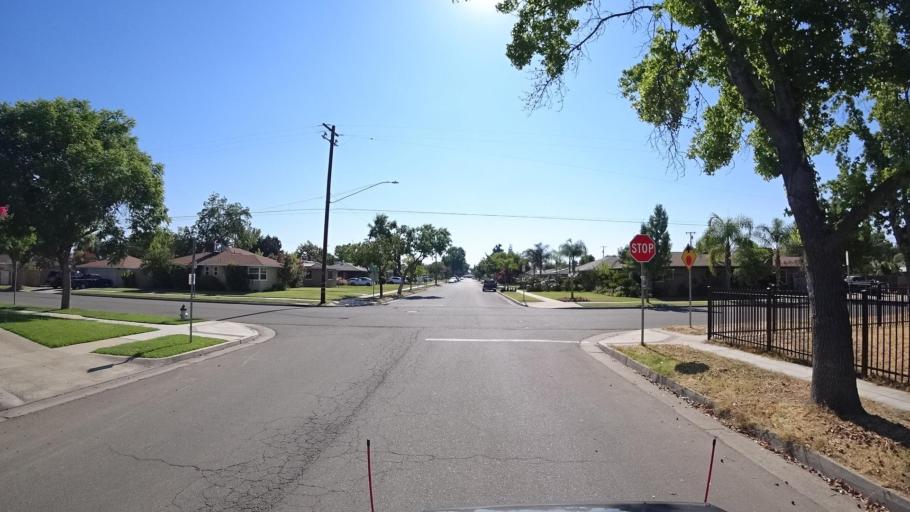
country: US
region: California
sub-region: Fresno County
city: Fresno
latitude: 36.7750
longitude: -119.7773
